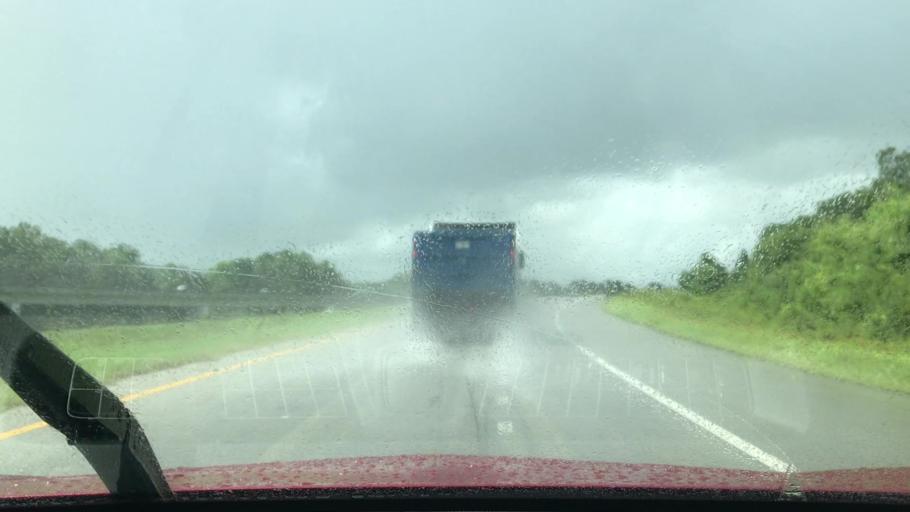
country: US
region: South Carolina
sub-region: Charleston County
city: Mount Pleasant
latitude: 32.8217
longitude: -79.8485
